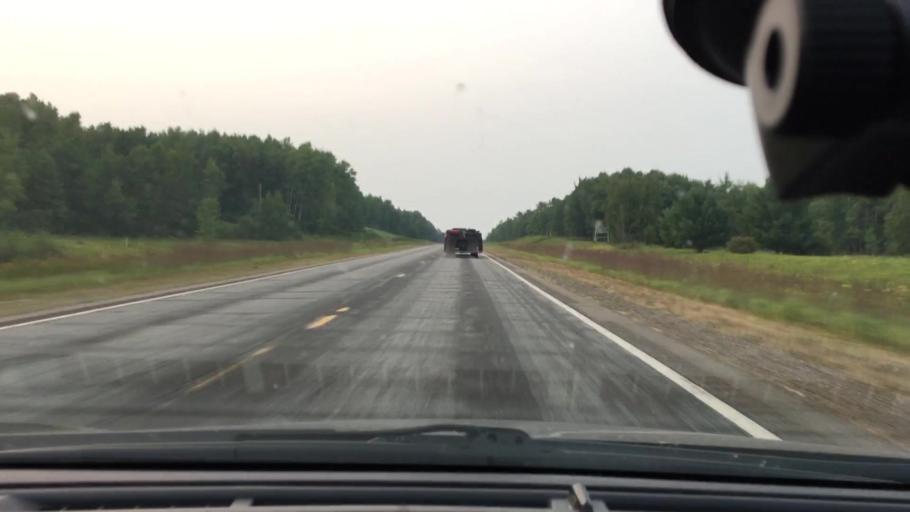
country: US
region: Minnesota
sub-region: Crow Wing County
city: Cross Lake
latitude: 46.7009
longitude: -93.9553
